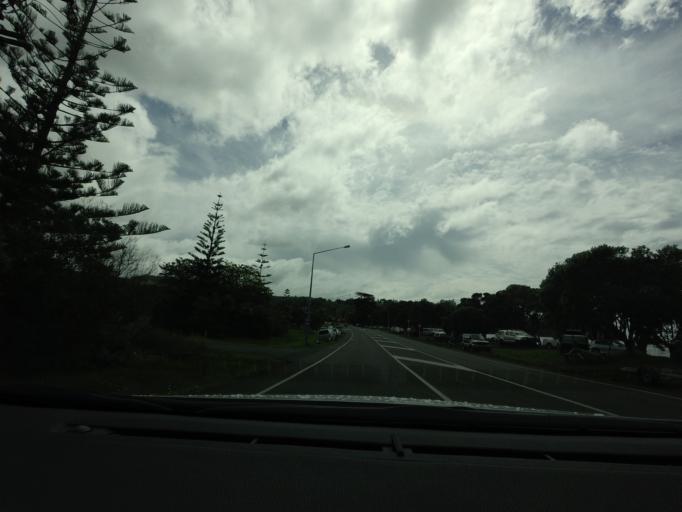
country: NZ
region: Auckland
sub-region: Auckland
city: Rothesay Bay
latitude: -36.5656
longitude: 174.6942
